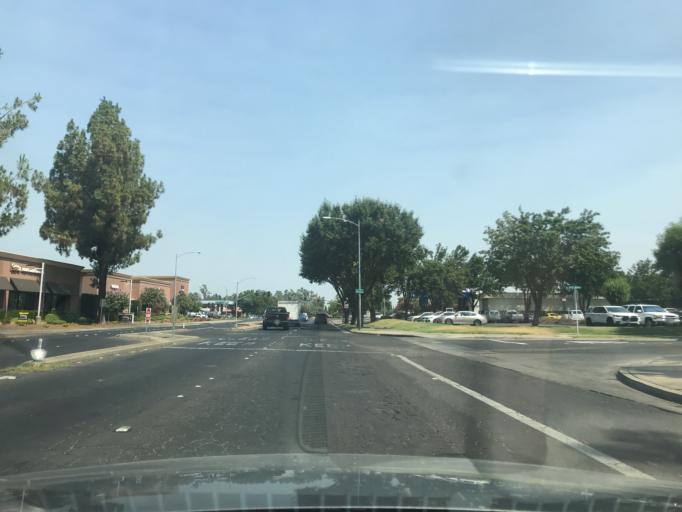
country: US
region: California
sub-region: Merced County
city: Merced
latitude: 37.3177
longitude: -120.4865
